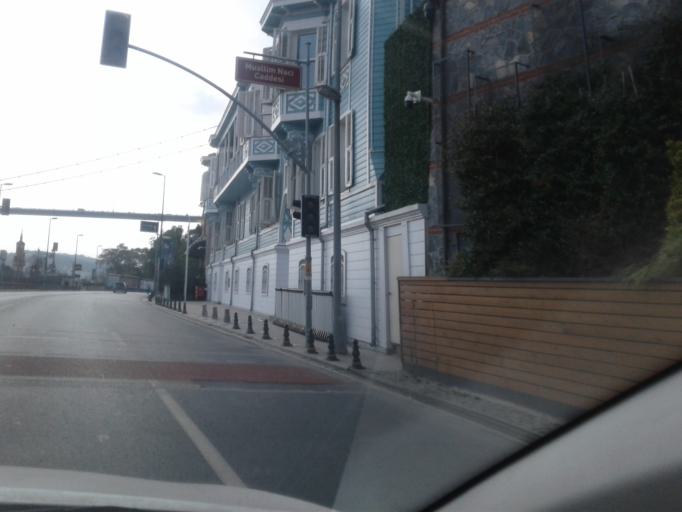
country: TR
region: Istanbul
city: UEskuedar
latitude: 41.0525
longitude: 29.0335
